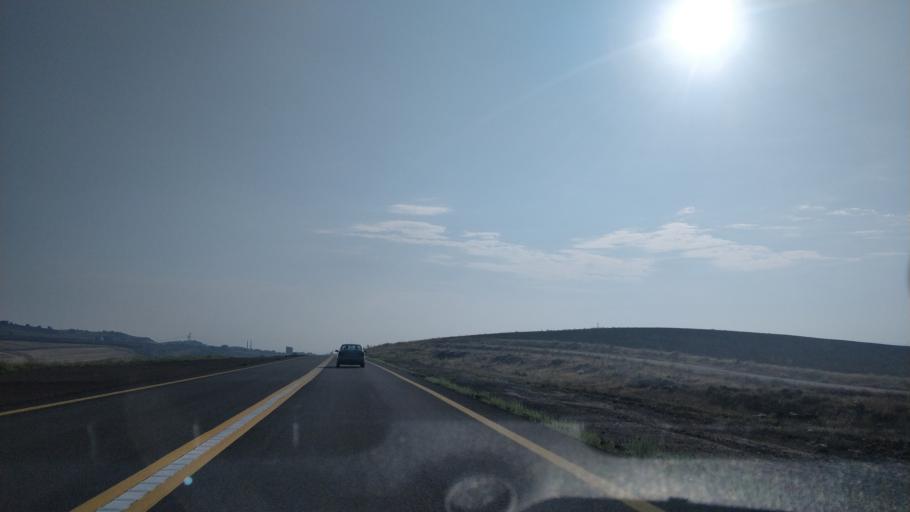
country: TR
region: Ankara
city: Etimesgut
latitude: 39.8536
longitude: 32.5637
